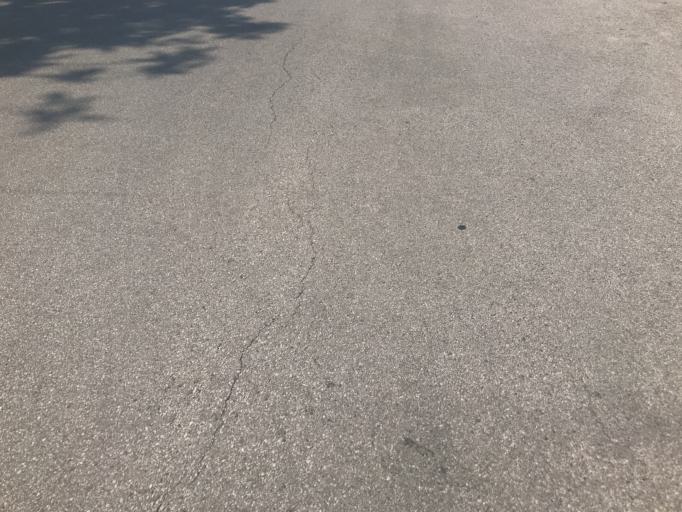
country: US
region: Texas
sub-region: Travis County
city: Austin
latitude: 30.3066
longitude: -97.7470
